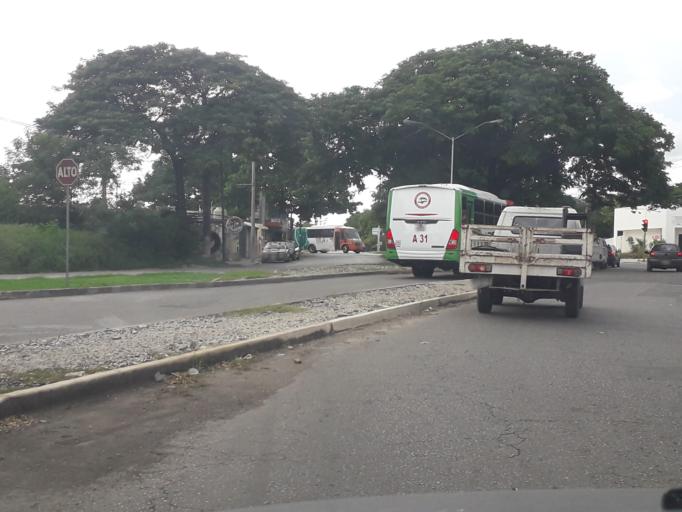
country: MX
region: Yucatan
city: Merida
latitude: 20.9733
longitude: -89.6624
